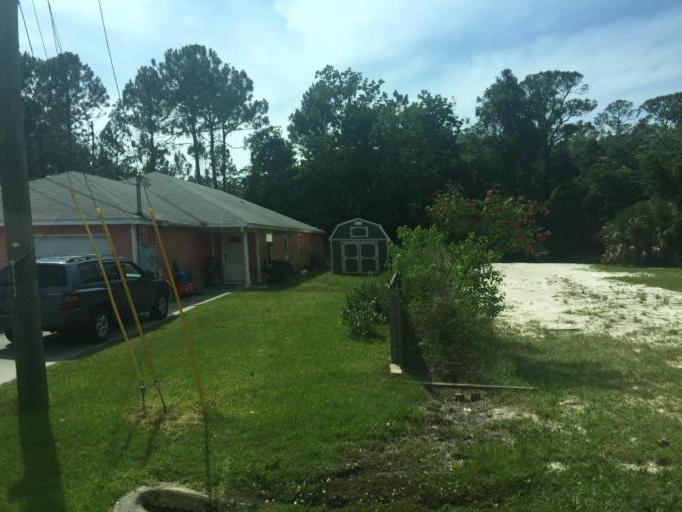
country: US
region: Florida
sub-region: Bay County
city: Laguna Beach
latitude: 30.2473
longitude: -85.9178
